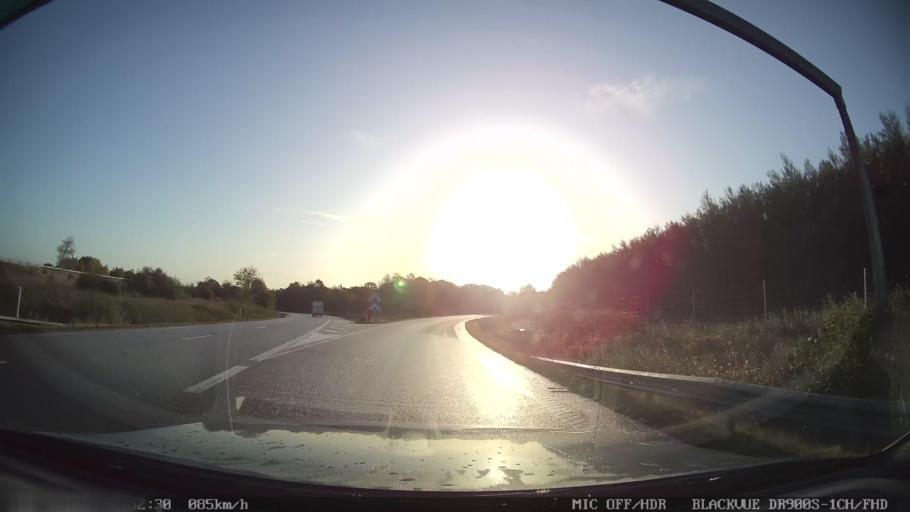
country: SE
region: Skane
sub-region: Helsingborg
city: Odakra
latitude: 56.0861
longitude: 12.7740
